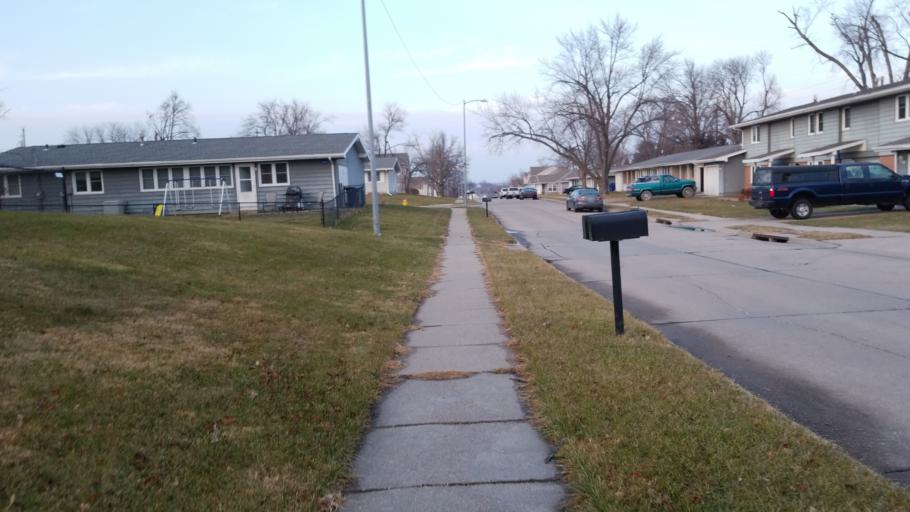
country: US
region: Nebraska
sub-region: Sarpy County
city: Offutt Air Force Base
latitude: 41.1215
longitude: -95.9481
